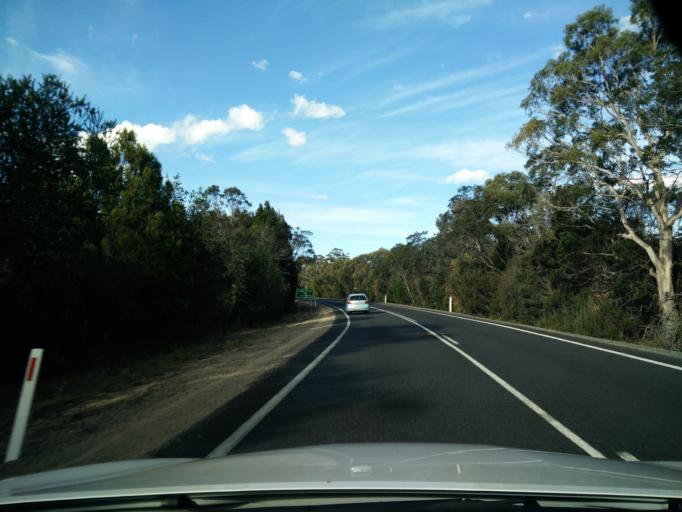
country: AU
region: Tasmania
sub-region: Break O'Day
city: St Helens
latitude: -42.0036
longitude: 148.2468
